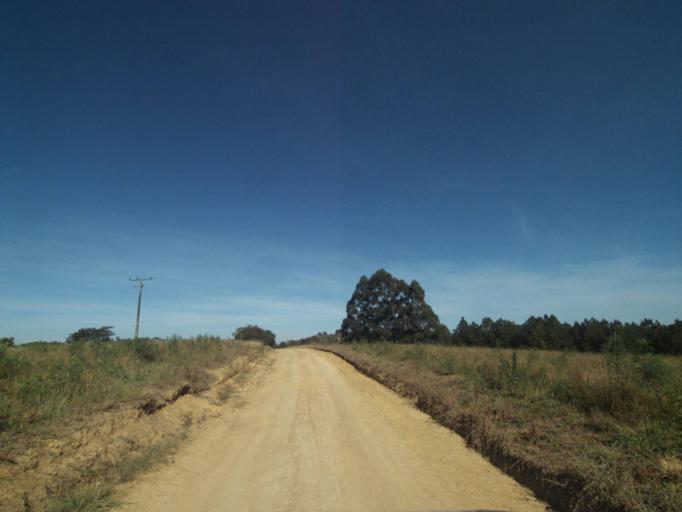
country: BR
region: Parana
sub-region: Tibagi
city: Tibagi
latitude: -24.5614
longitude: -50.4723
